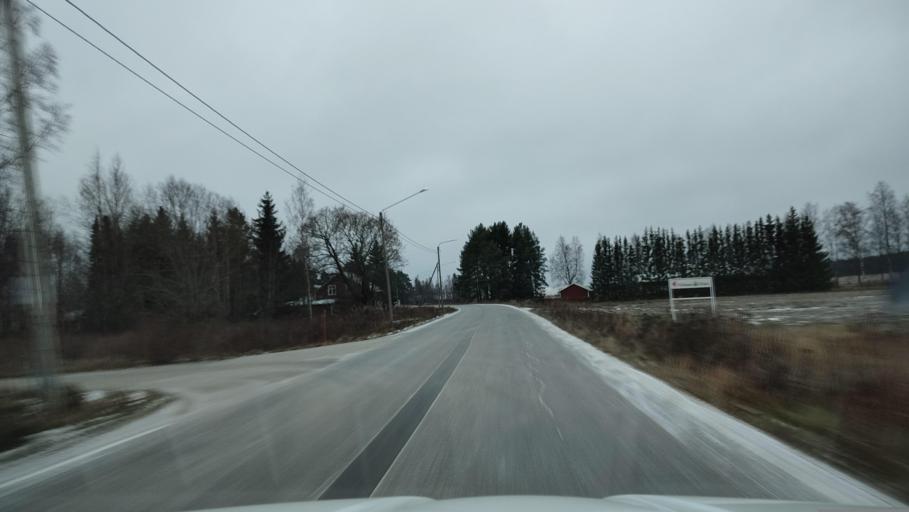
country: FI
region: Southern Ostrobothnia
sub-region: Suupohja
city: Karijoki
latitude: 62.2506
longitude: 21.6733
